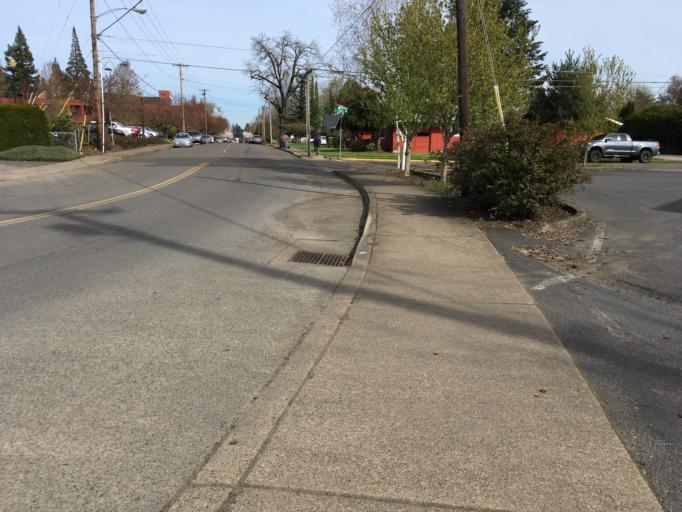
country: US
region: Oregon
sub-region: Yamhill County
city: McMinnville
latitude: 45.2003
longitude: -123.2039
